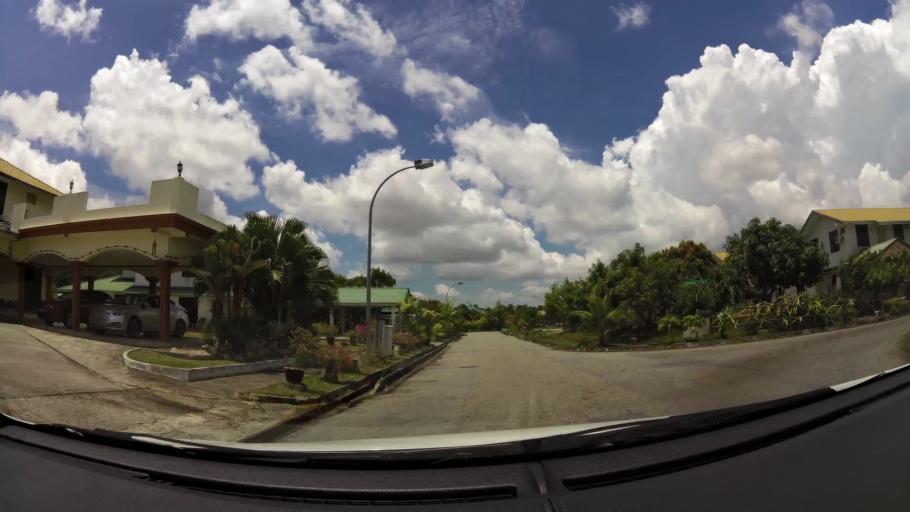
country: BN
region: Brunei and Muara
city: Bandar Seri Begawan
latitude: 4.9611
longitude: 114.9165
